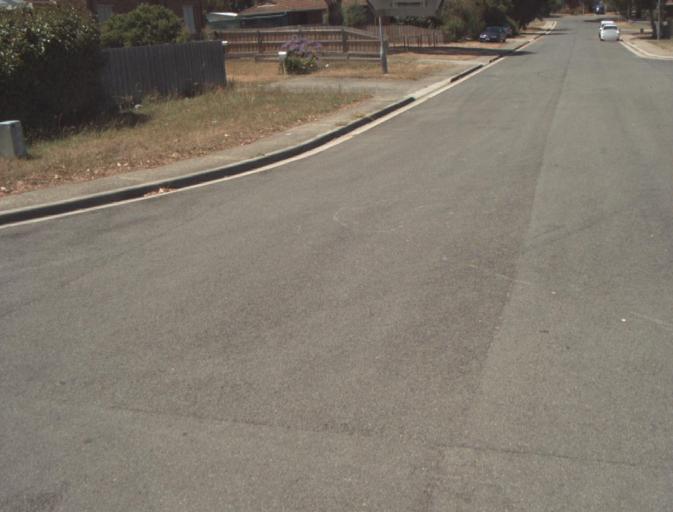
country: AU
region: Tasmania
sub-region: Launceston
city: Mayfield
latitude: -41.3799
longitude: 147.1328
